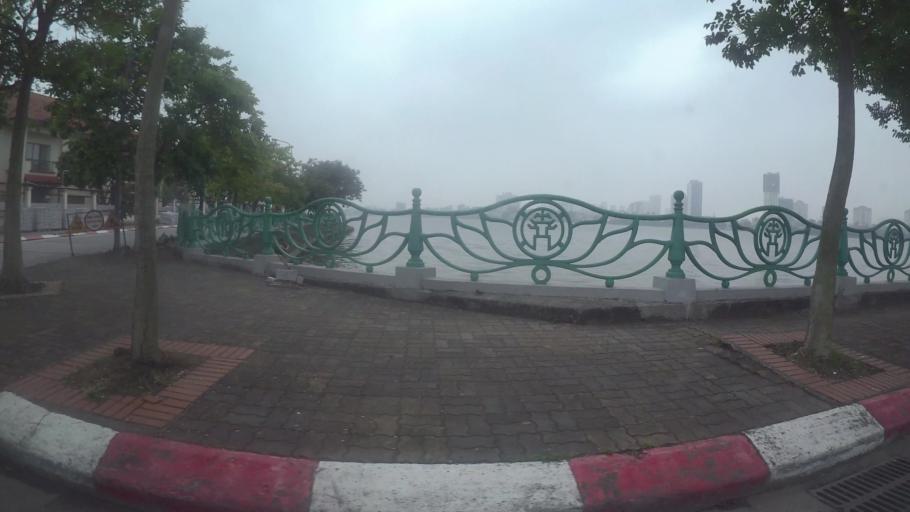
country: VN
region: Ha Noi
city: Tay Ho
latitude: 21.0670
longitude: 105.8190
